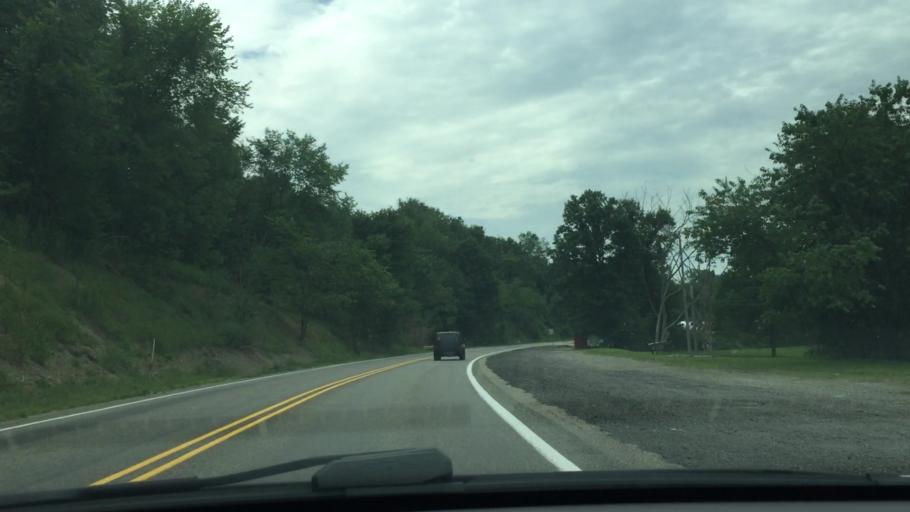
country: US
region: Pennsylvania
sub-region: Allegheny County
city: Oakdale
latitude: 40.4163
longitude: -80.1900
